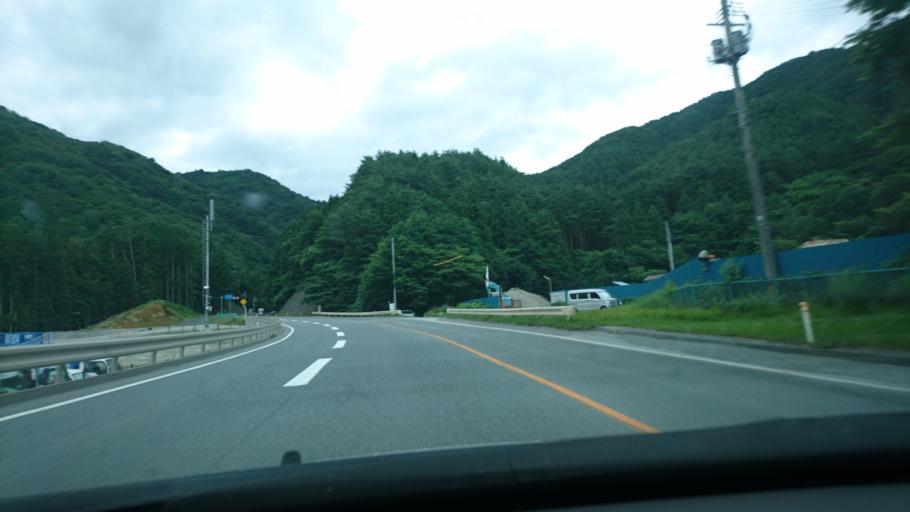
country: JP
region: Iwate
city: Kamaishi
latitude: 39.2182
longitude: 141.8738
